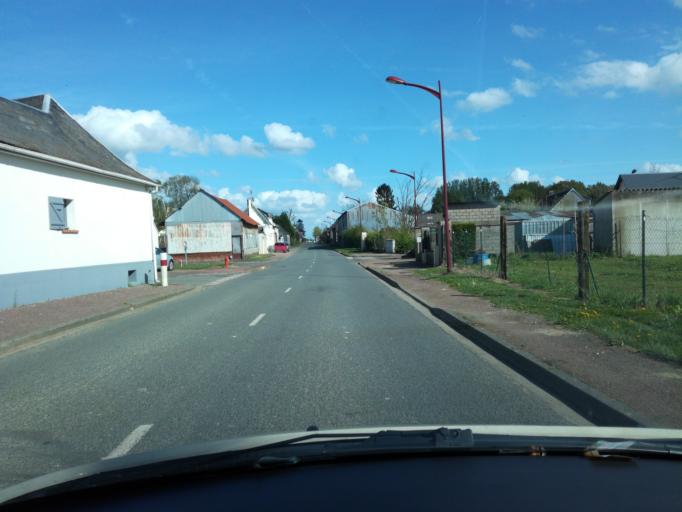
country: FR
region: Picardie
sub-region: Departement de la Somme
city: Hornoy-le-Bourg
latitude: 49.8274
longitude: 1.9371
